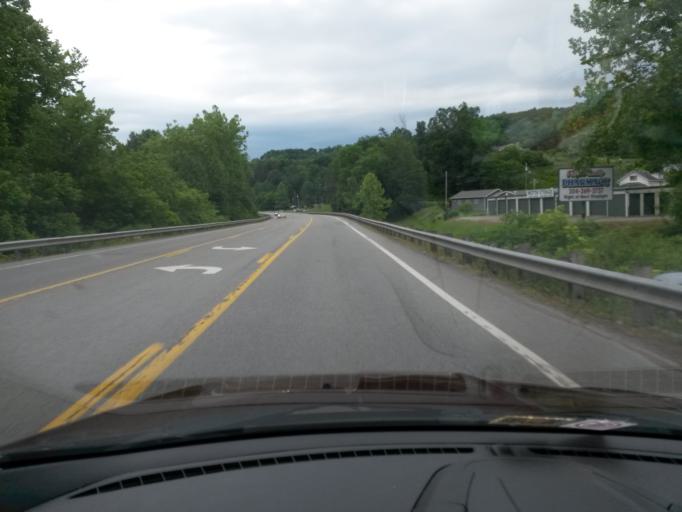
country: US
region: West Virginia
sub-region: Lewis County
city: Weston
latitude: 39.0292
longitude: -80.4347
